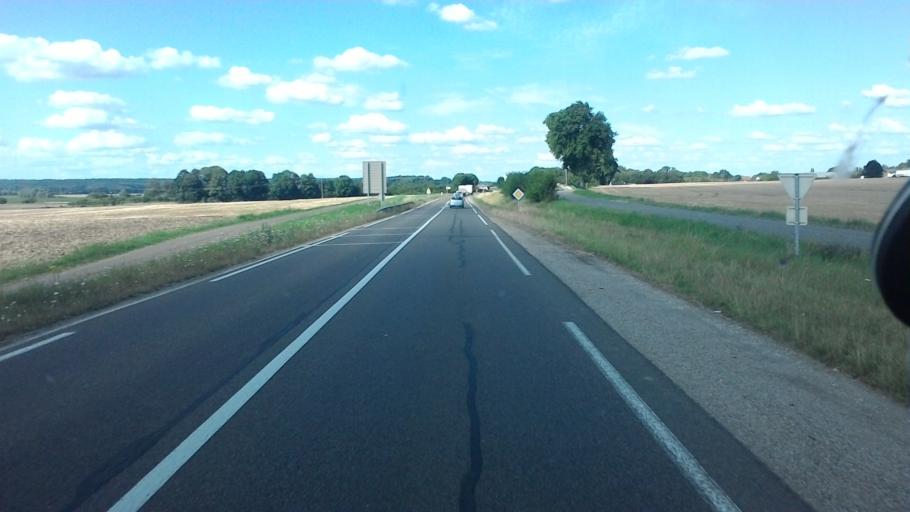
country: FR
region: Franche-Comte
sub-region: Departement de la Haute-Saone
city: Gy
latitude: 47.4029
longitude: 5.7999
